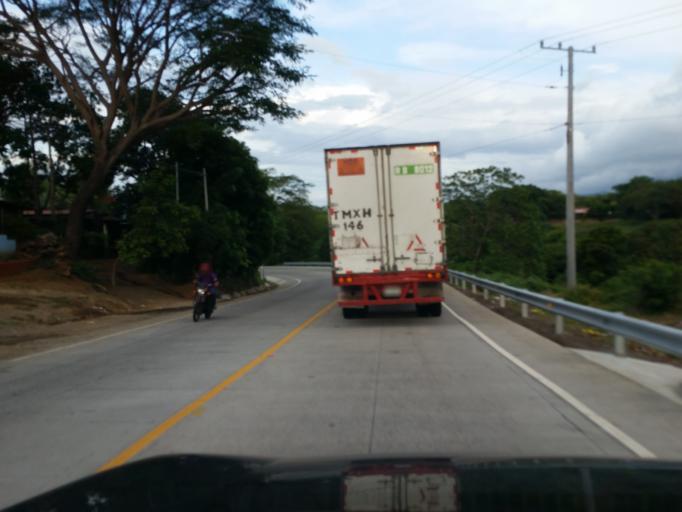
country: NI
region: Managua
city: Ciudad Sandino
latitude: 12.0812
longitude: -86.3630
